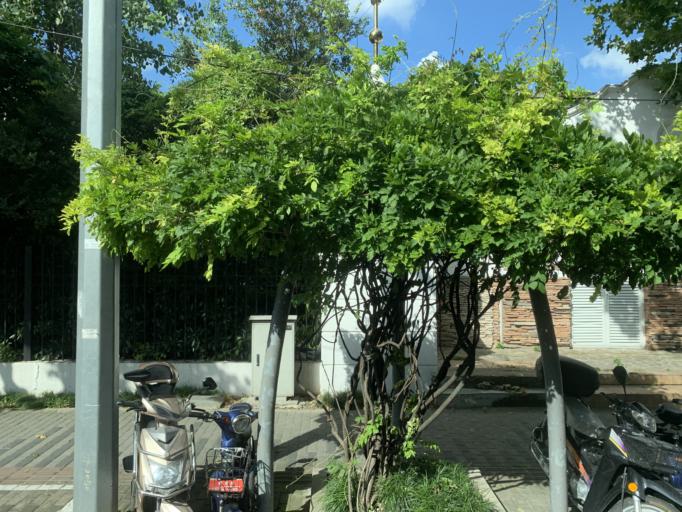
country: CN
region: Shanghai Shi
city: Pudong
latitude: 31.2475
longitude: 121.5611
